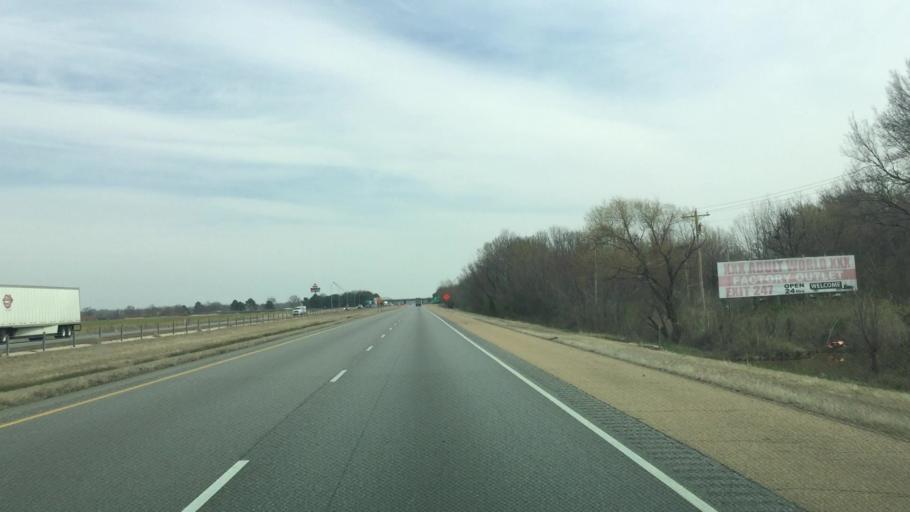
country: US
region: Arkansas
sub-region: Saint Francis County
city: Forrest City
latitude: 34.9794
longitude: -90.9148
